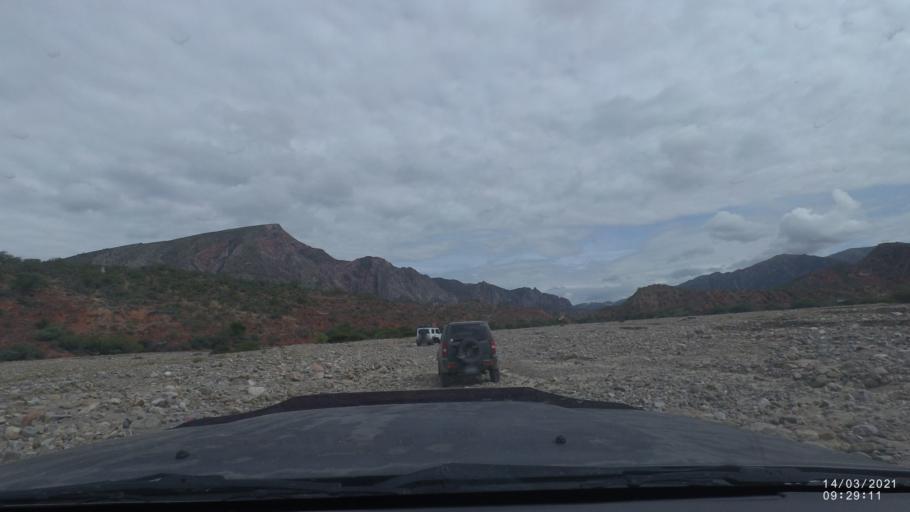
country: BO
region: Cochabamba
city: Cliza
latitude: -17.9474
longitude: -65.8566
